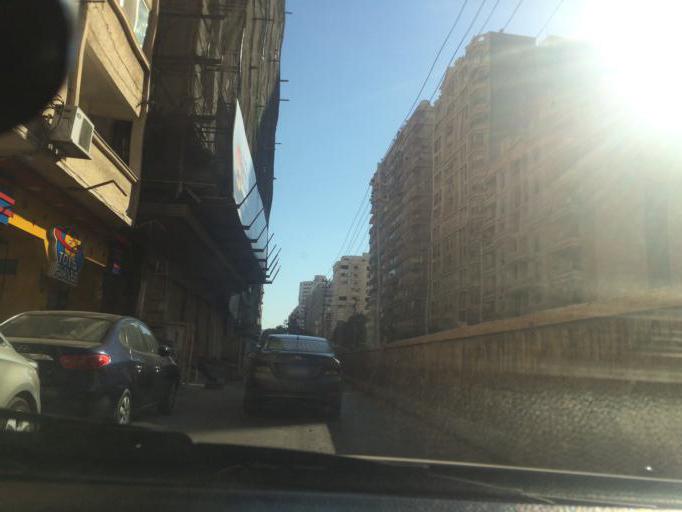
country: EG
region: Alexandria
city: Alexandria
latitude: 31.2298
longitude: 29.9535
